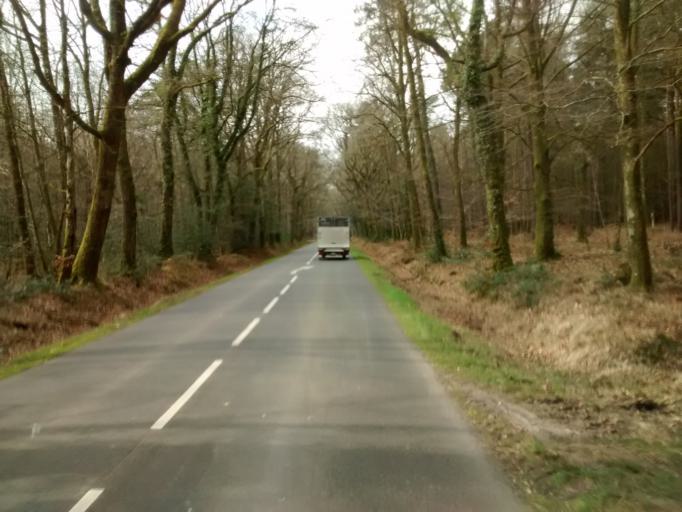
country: FR
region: Brittany
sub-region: Departement d'Ille-et-Vilaine
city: Paimpont
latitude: 48.0161
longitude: -2.1533
